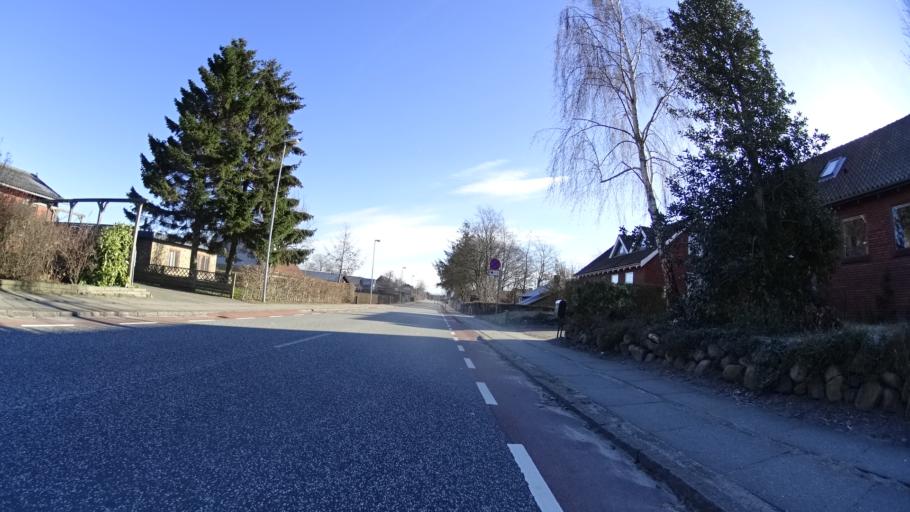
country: DK
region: Central Jutland
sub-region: Arhus Kommune
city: Kolt
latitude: 56.1074
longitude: 10.0934
